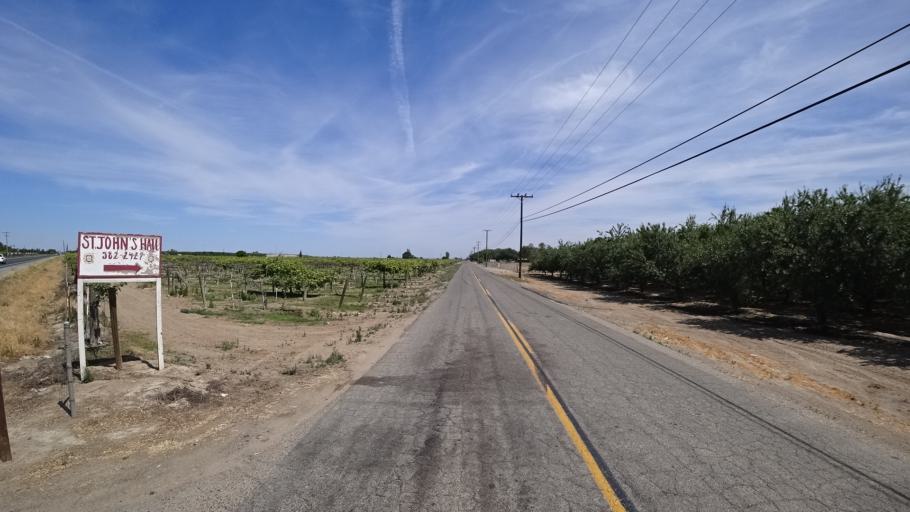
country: US
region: California
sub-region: Kings County
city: Hanford
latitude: 36.3515
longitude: -119.6101
